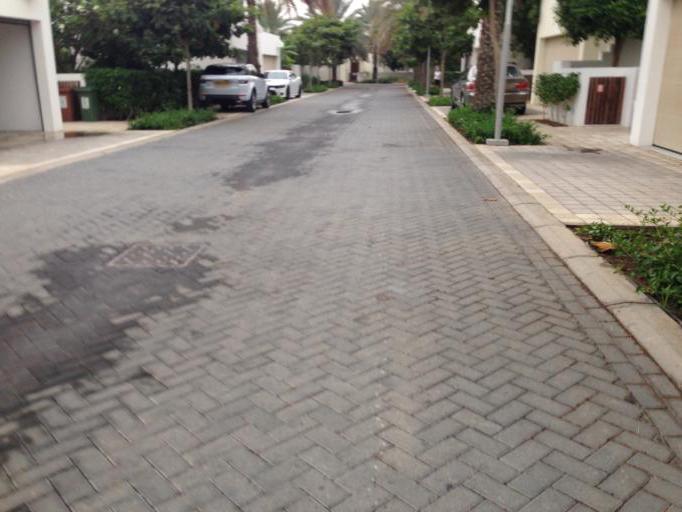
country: OM
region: Muhafazat Masqat
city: As Sib al Jadidah
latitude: 23.6262
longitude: 58.2657
